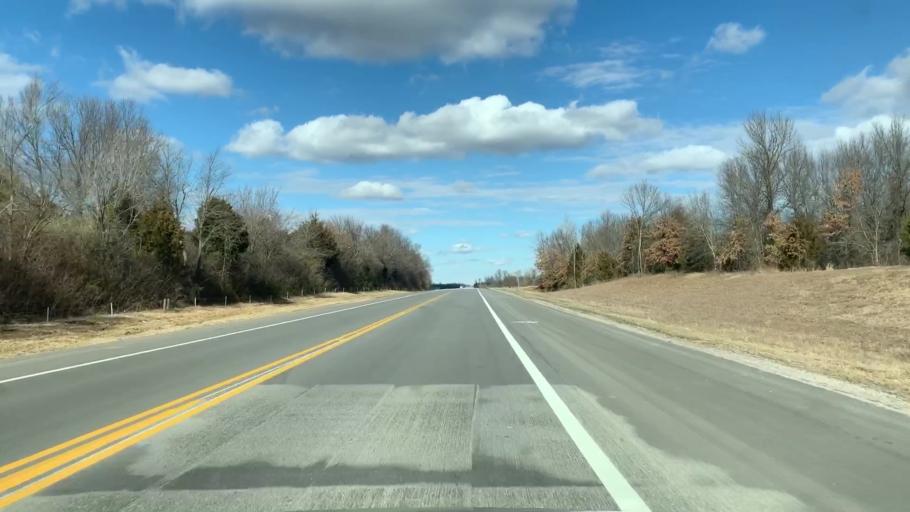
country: US
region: Kansas
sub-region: Cherokee County
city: Columbus
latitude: 37.2556
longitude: -94.8318
